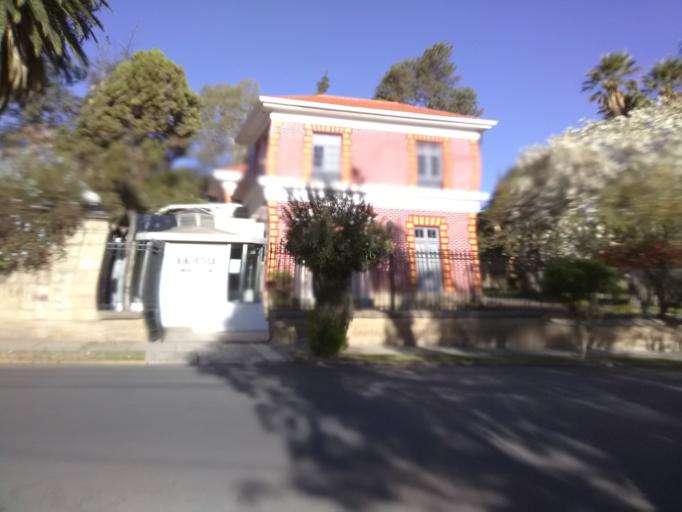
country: BO
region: Cochabamba
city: Cochabamba
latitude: -17.3741
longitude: -66.1538
